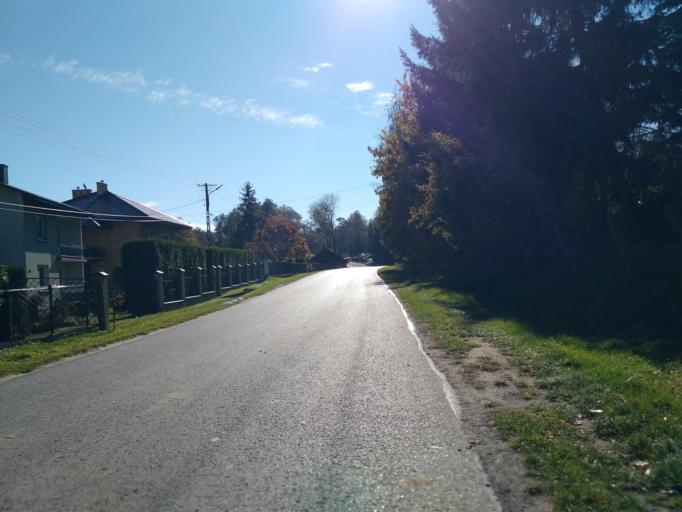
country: PL
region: Subcarpathian Voivodeship
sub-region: Powiat ropczycko-sedziszowski
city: Iwierzyce
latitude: 49.9872
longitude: 21.7262
